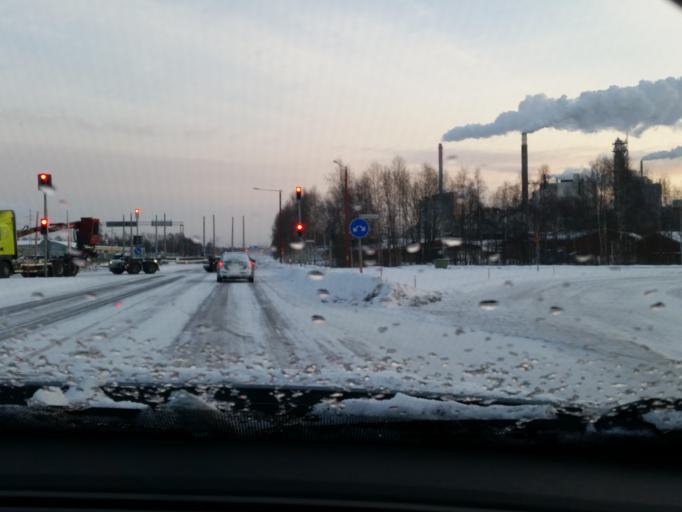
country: SE
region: Norrbotten
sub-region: Pitea Kommun
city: Pitea
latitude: 65.3191
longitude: 21.4358
